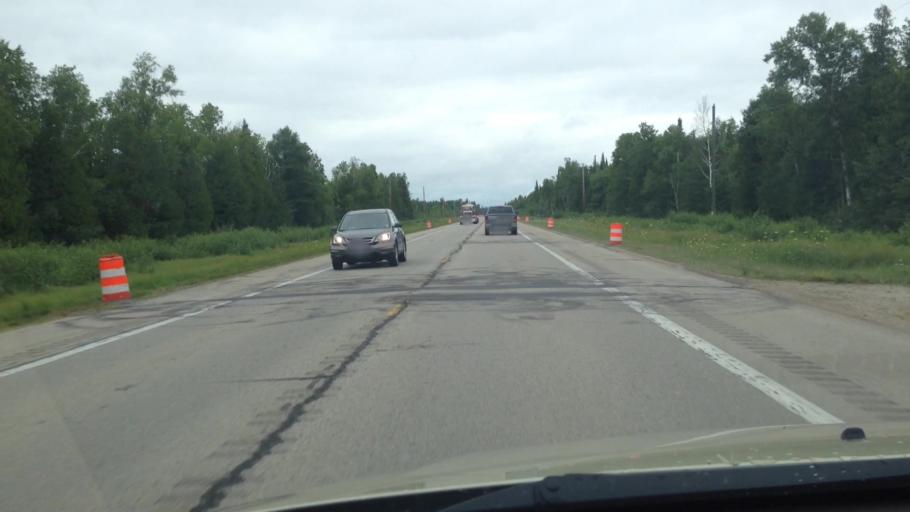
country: US
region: Michigan
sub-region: Delta County
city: Escanaba
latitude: 45.6154
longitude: -87.2150
